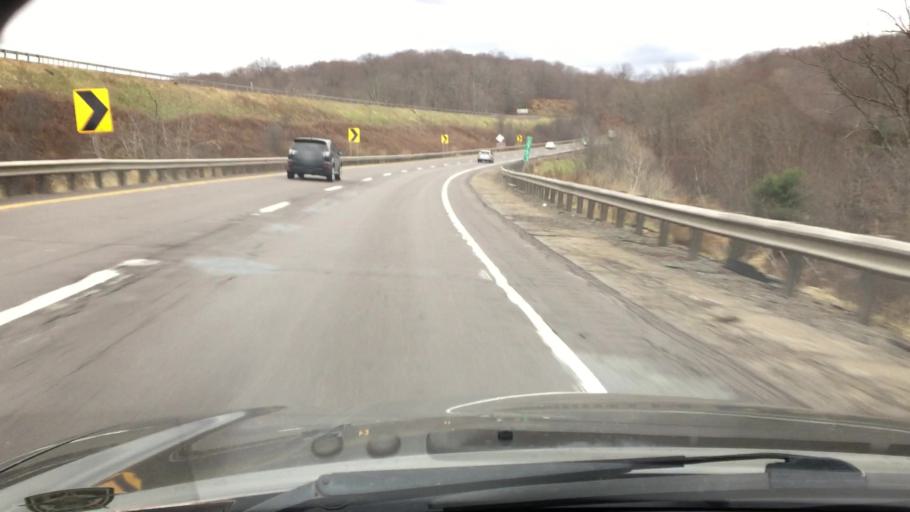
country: US
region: Pennsylvania
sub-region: Luzerne County
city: White Haven
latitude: 41.0563
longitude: -75.7248
